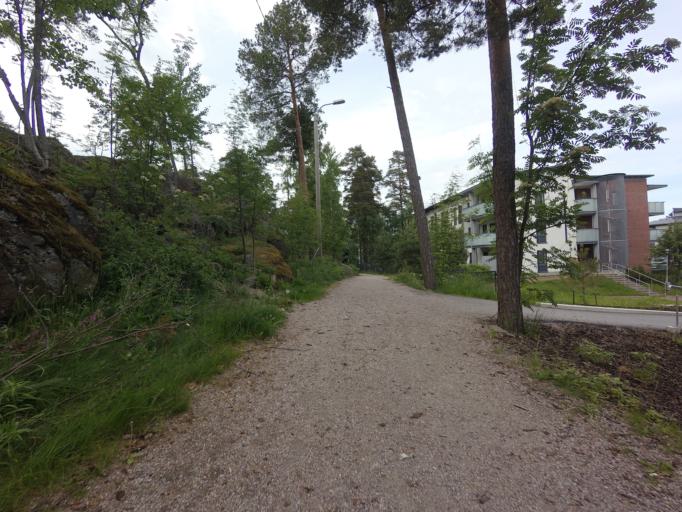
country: FI
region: Uusimaa
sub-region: Helsinki
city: Koukkuniemi
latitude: 60.1535
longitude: 24.7543
